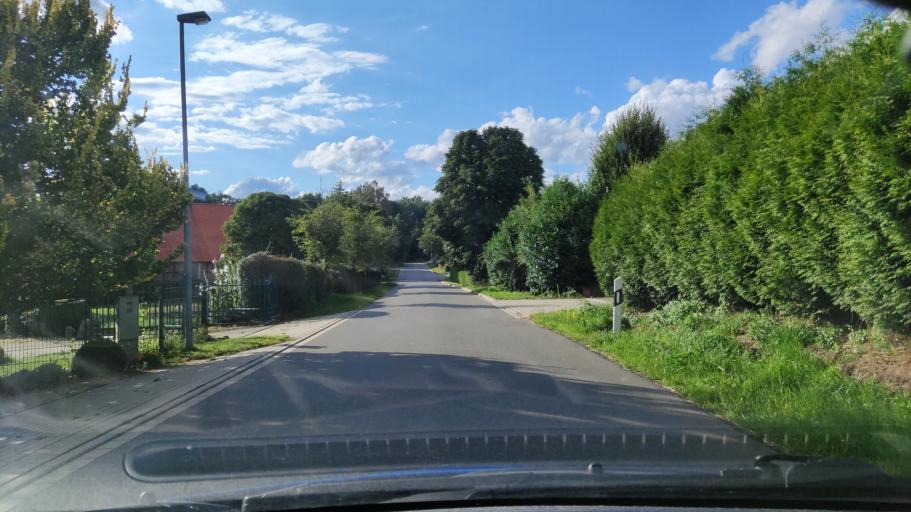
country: DE
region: Lower Saxony
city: Boitze
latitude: 53.1579
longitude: 10.7390
